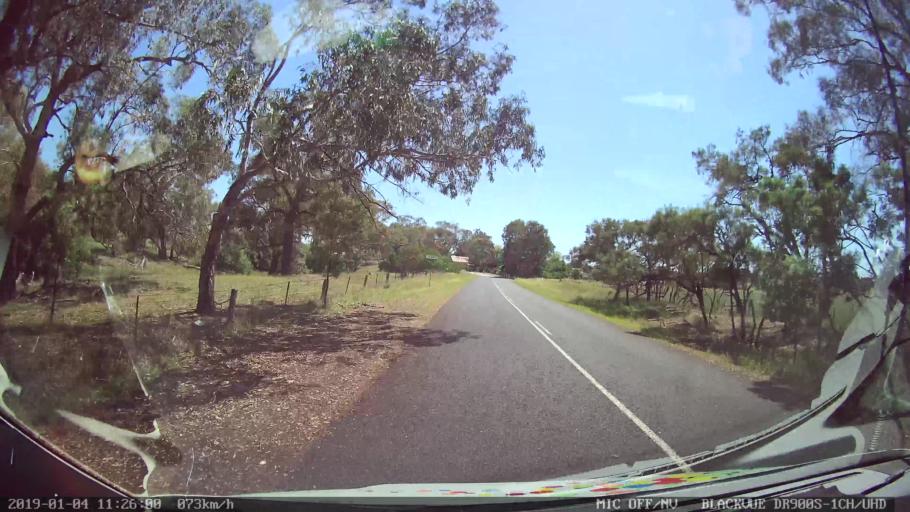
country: AU
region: New South Wales
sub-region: Cabonne
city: Molong
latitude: -33.1185
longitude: 148.7545
